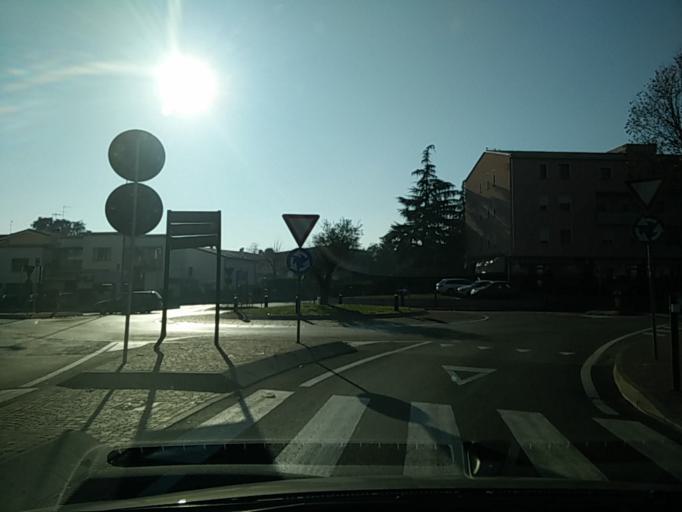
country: IT
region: Veneto
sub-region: Provincia di Treviso
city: Silea
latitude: 45.6538
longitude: 12.2960
